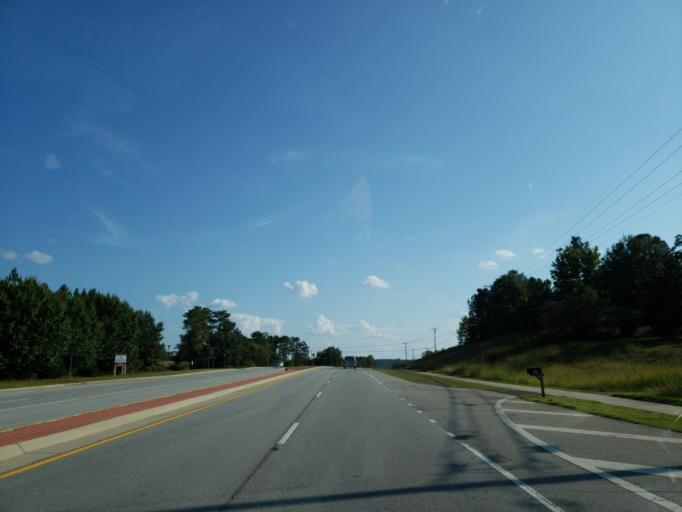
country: US
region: Georgia
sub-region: Paulding County
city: Hiram
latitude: 33.8937
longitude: -84.7798
